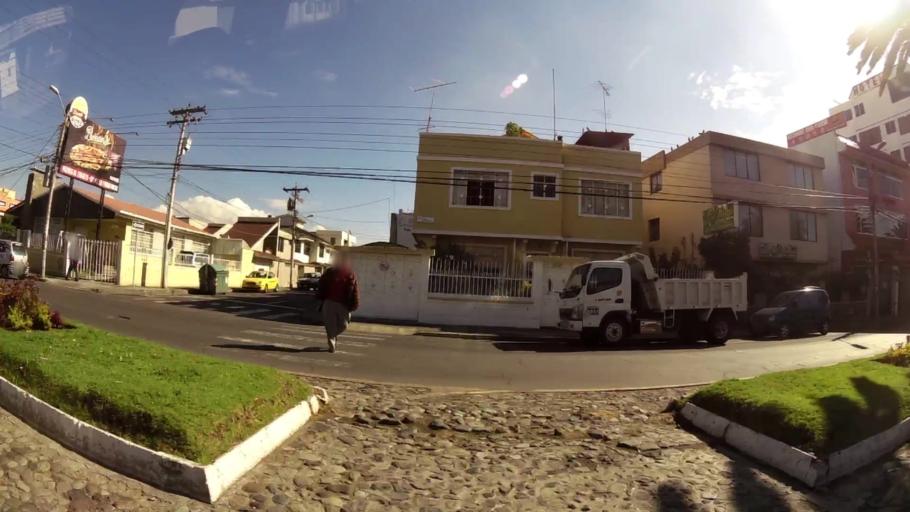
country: EC
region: Chimborazo
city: Riobamba
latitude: -1.6633
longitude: -78.6608
